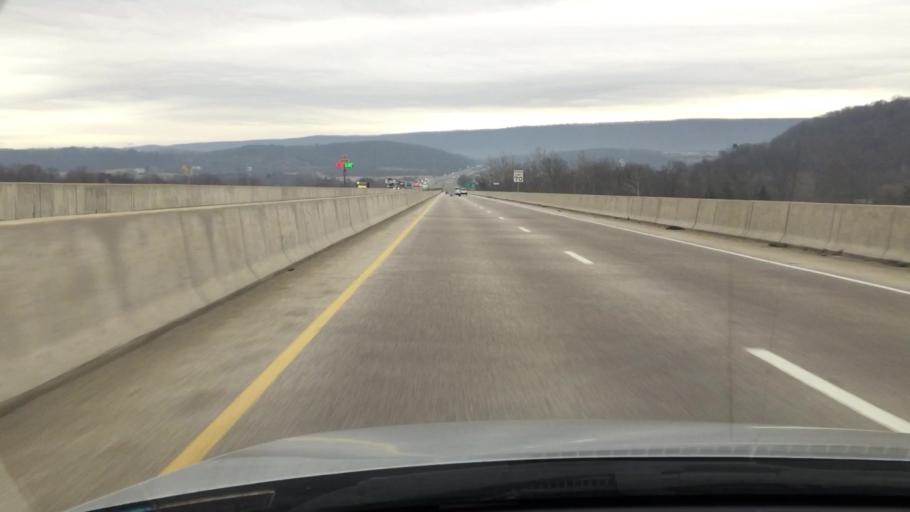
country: US
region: Pennsylvania
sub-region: Columbia County
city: Mifflinville
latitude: 41.0292
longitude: -76.3278
